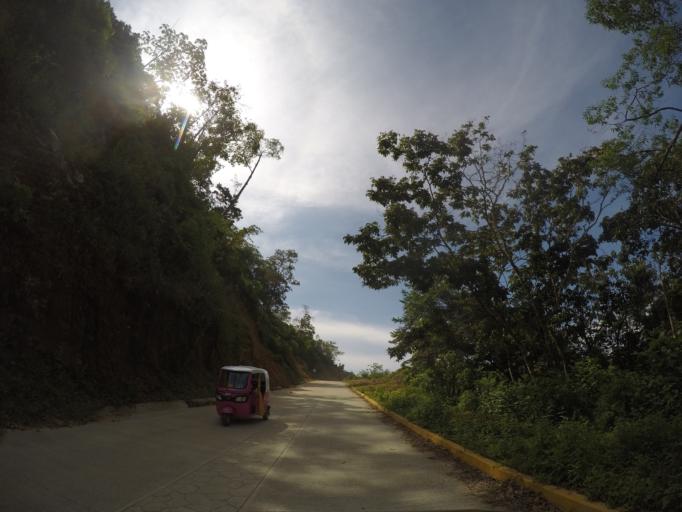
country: MX
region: Oaxaca
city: Pluma Hidalgo
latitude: 15.9310
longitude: -96.4207
